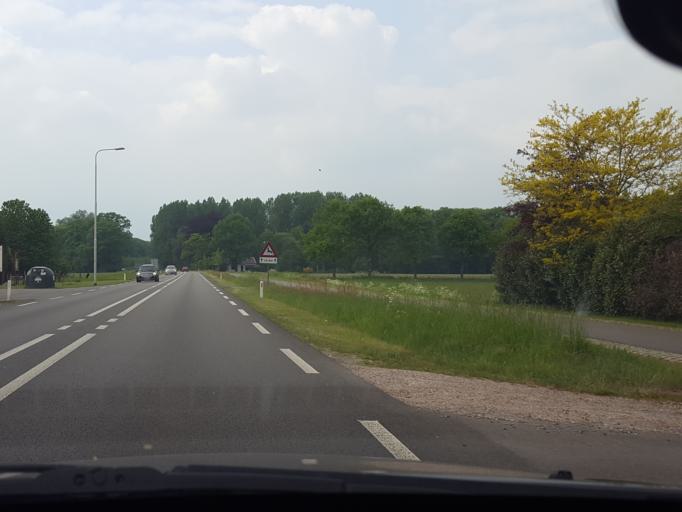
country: NL
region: Gelderland
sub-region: Gemeente Winterswijk
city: Winterswijk
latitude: 51.9533
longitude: 6.7500
